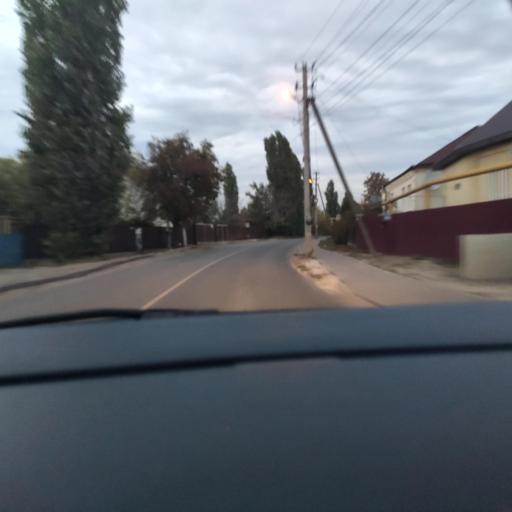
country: RU
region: Voronezj
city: Podgornoye
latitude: 51.7300
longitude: 39.1376
